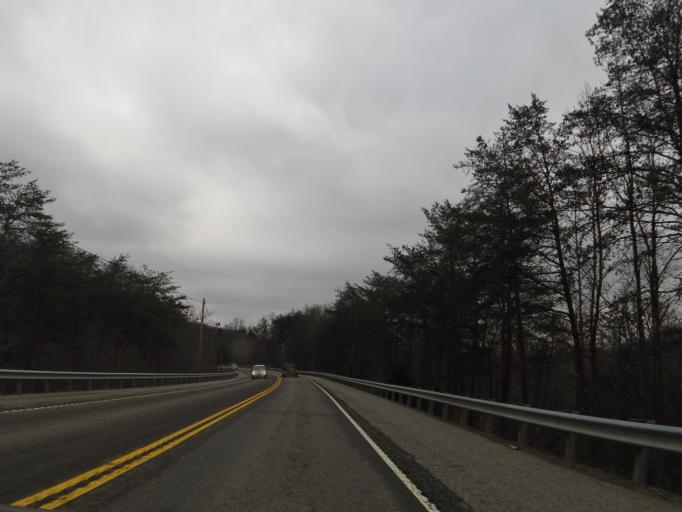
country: US
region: Tennessee
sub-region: Campbell County
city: Jacksboro
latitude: 36.3926
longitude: -84.2638
